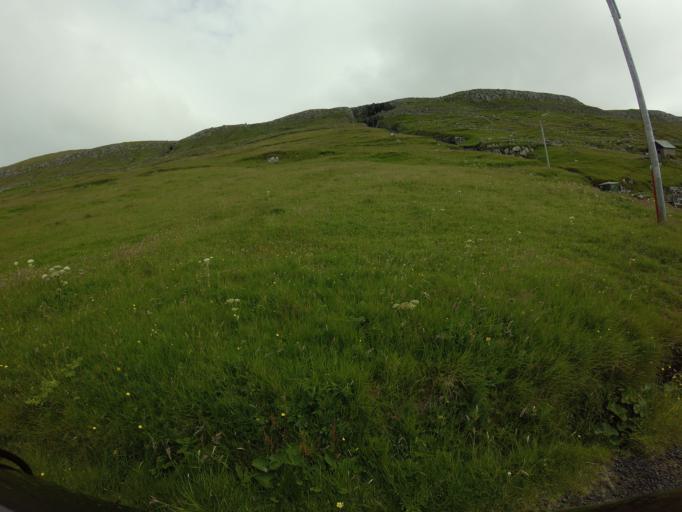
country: FO
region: Sandoy
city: Sandur
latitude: 61.7943
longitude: -6.7483
